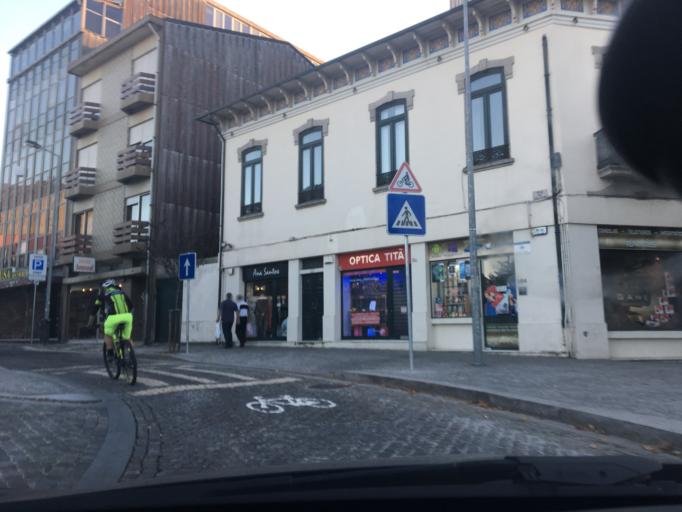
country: PT
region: Porto
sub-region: Matosinhos
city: Matosinhos
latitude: 41.1867
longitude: -8.6923
